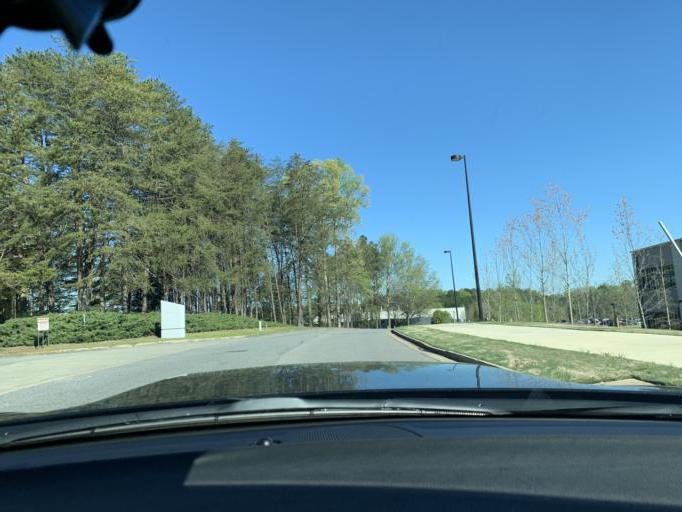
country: US
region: Georgia
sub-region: Fulton County
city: Alpharetta
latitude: 34.0834
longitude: -84.2533
